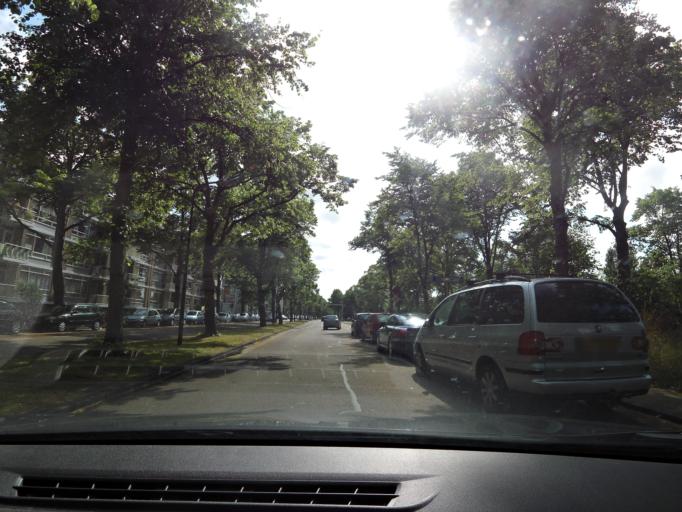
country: NL
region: South Holland
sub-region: Gemeente Den Haag
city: The Hague
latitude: 52.0469
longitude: 4.2811
